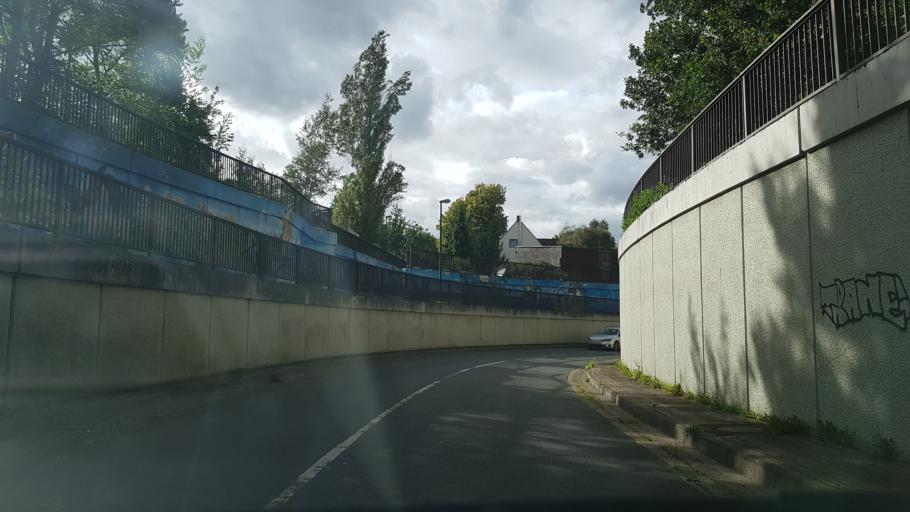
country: DE
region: Lower Saxony
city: Oyten
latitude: 53.0318
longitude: 8.9700
